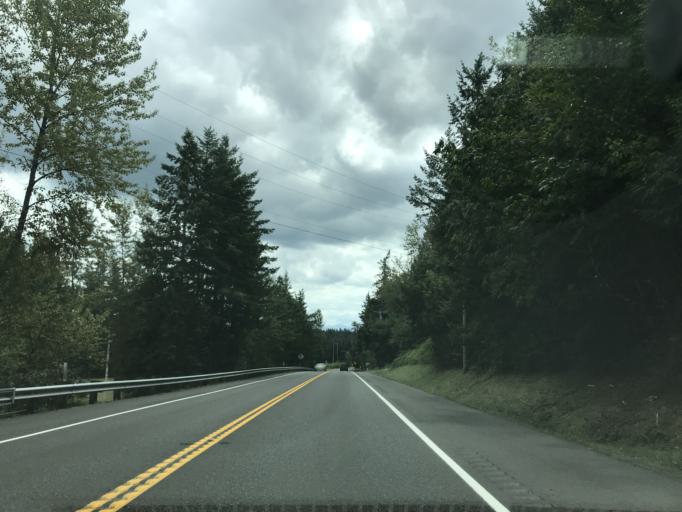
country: US
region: Washington
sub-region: King County
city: Maple Valley
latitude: 47.4028
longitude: -122.0478
